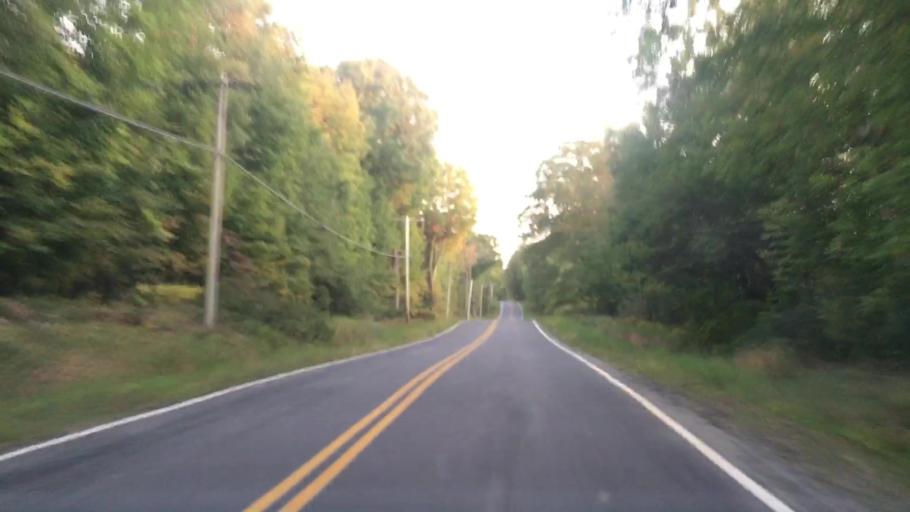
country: US
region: Maine
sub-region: Somerset County
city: Cornville
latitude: 44.8607
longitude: -69.6832
